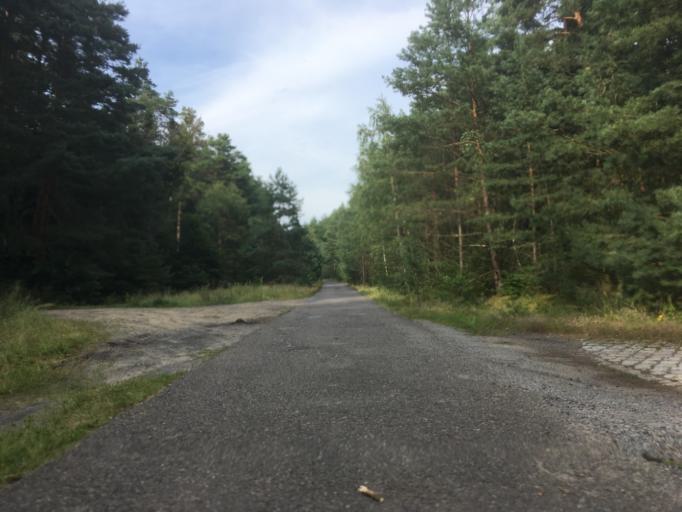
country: DE
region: Brandenburg
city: Melchow
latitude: 52.8049
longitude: 13.6988
